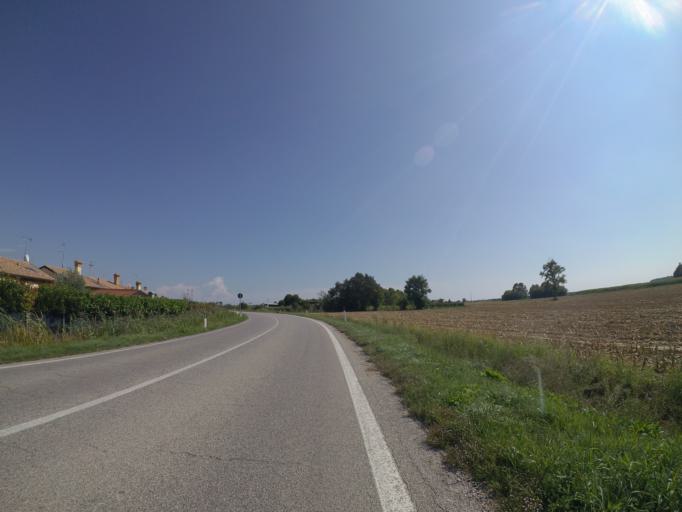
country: IT
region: Friuli Venezia Giulia
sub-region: Provincia di Udine
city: Carlino
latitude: 45.8086
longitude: 13.1632
